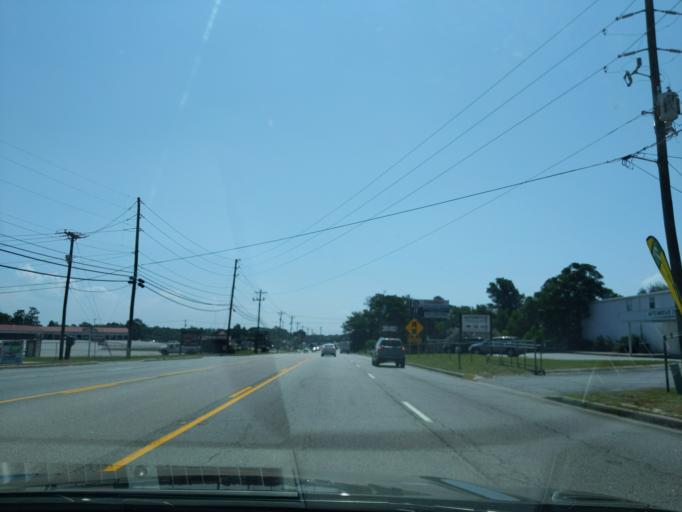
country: US
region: South Carolina
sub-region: Lexington County
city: Oak Grove
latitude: 33.9746
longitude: -81.1594
